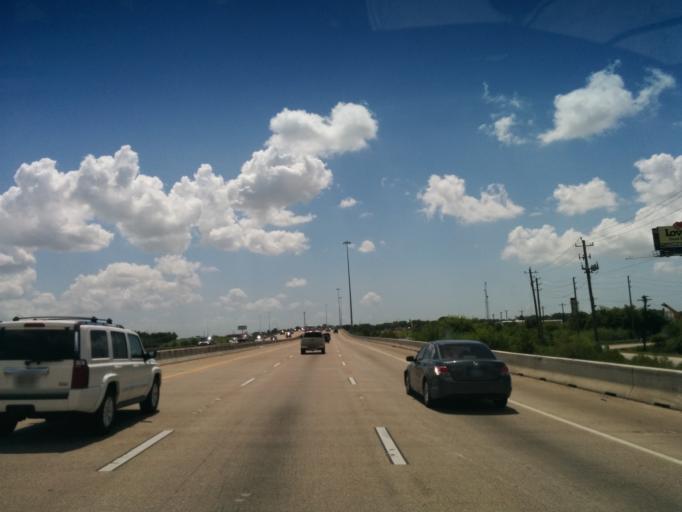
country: US
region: Texas
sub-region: Harris County
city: Highlands
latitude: 29.7945
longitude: -95.0658
